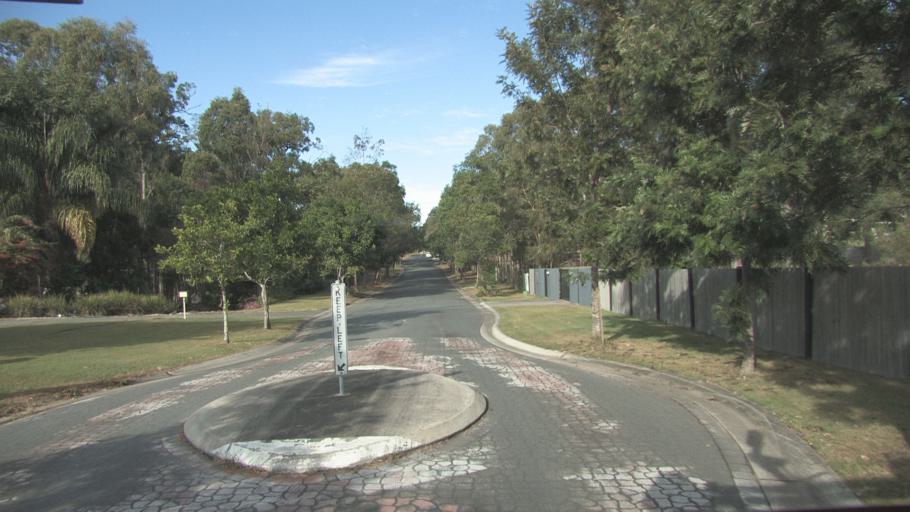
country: AU
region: Queensland
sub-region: Brisbane
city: Forest Lake
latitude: -27.6586
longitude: 153.0164
